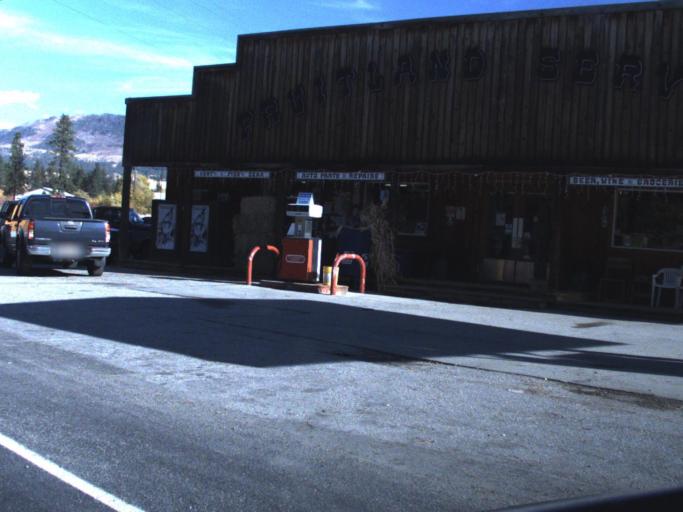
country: US
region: Washington
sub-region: Lincoln County
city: Davenport
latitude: 48.0715
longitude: -118.1983
